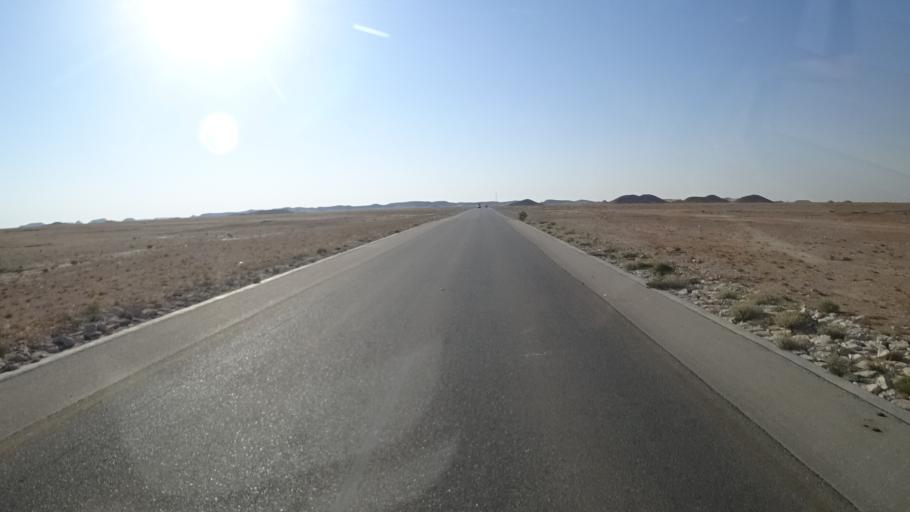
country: OM
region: Zufar
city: Salalah
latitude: 17.6391
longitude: 53.8801
